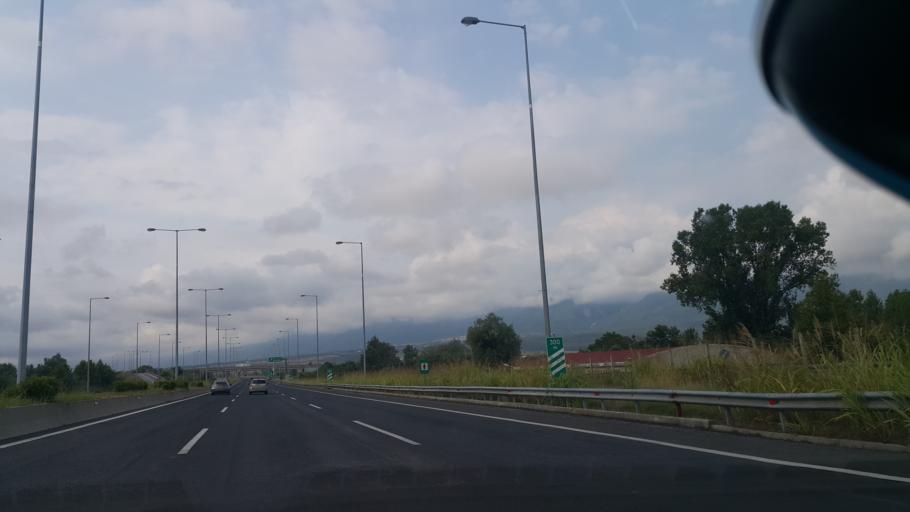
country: GR
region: Central Macedonia
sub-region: Nomos Pierias
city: Dion
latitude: 40.1556
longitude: 22.5429
